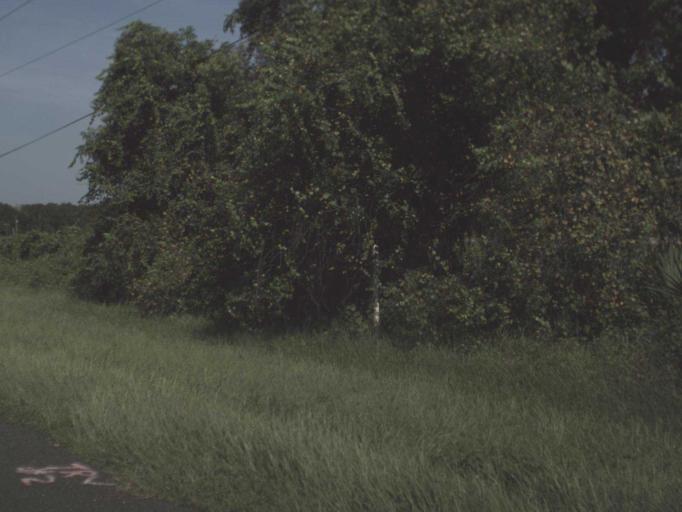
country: US
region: Florida
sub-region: Hillsborough County
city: Plant City
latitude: 27.9379
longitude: -82.1048
